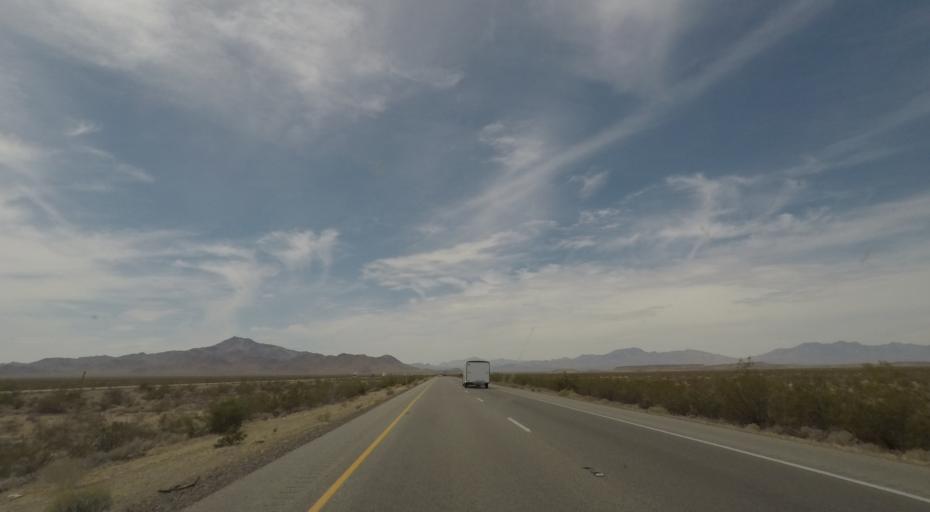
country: US
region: California
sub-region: San Bernardino County
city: Needles
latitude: 34.8059
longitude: -115.2645
